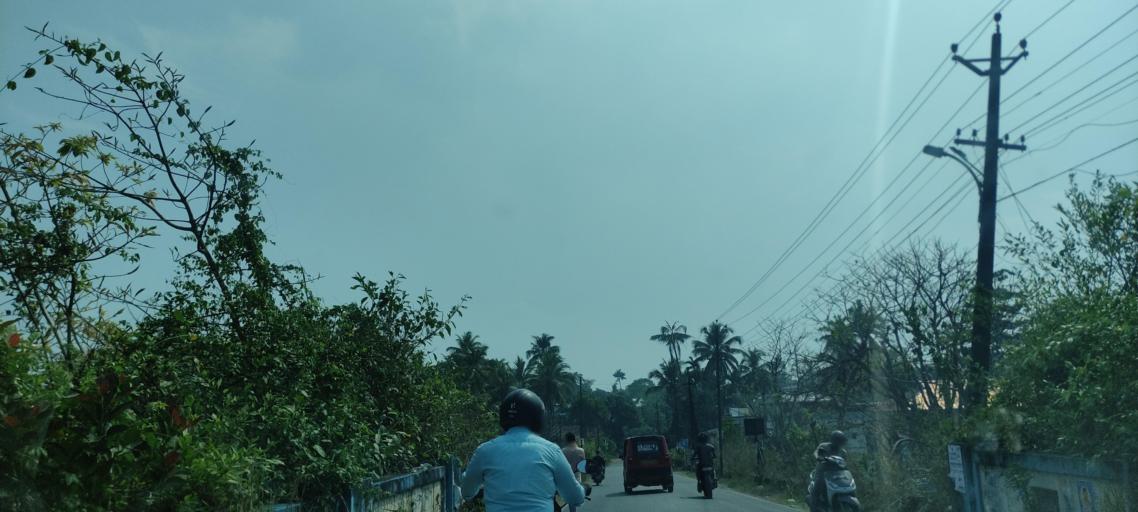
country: IN
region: Kerala
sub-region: Alappuzha
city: Kutiatodu
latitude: 9.8229
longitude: 76.3061
